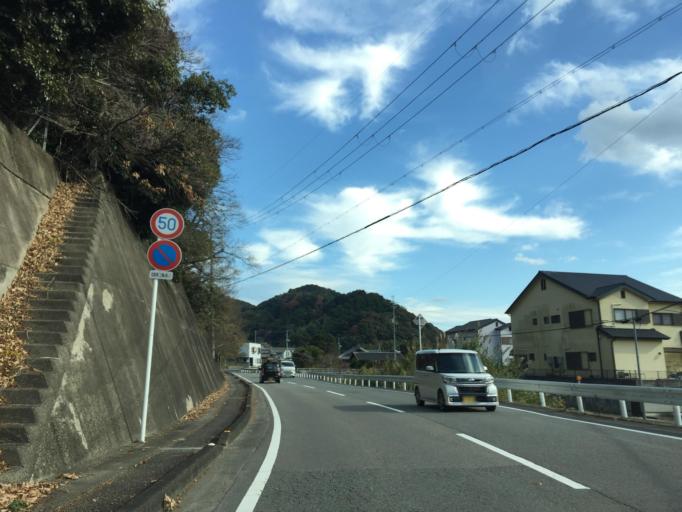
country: JP
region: Wakayama
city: Kainan
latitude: 34.1633
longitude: 135.2544
